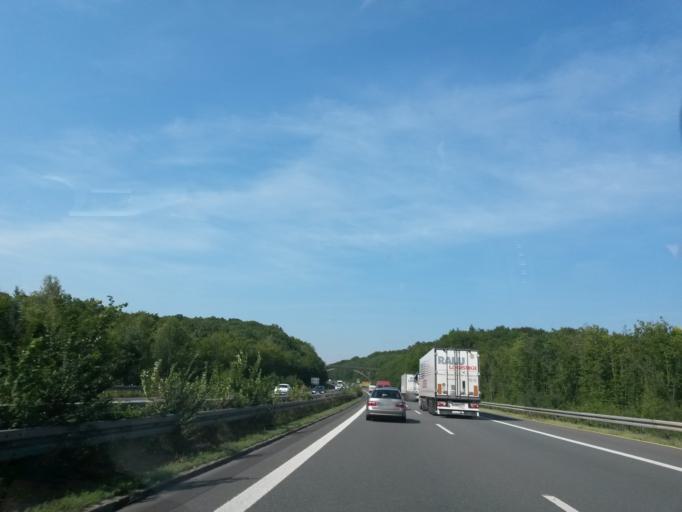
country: DE
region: Bavaria
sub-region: Regierungsbezirk Unterfranken
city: Unterpleichfeld
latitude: 49.8889
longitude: 9.9996
